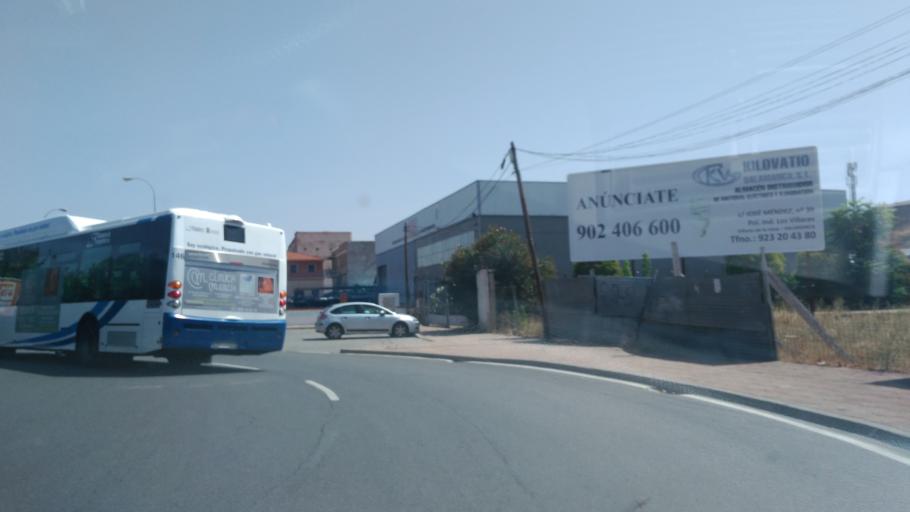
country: ES
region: Castille and Leon
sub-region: Provincia de Salamanca
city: Salamanca
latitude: 40.9548
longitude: -5.6859
